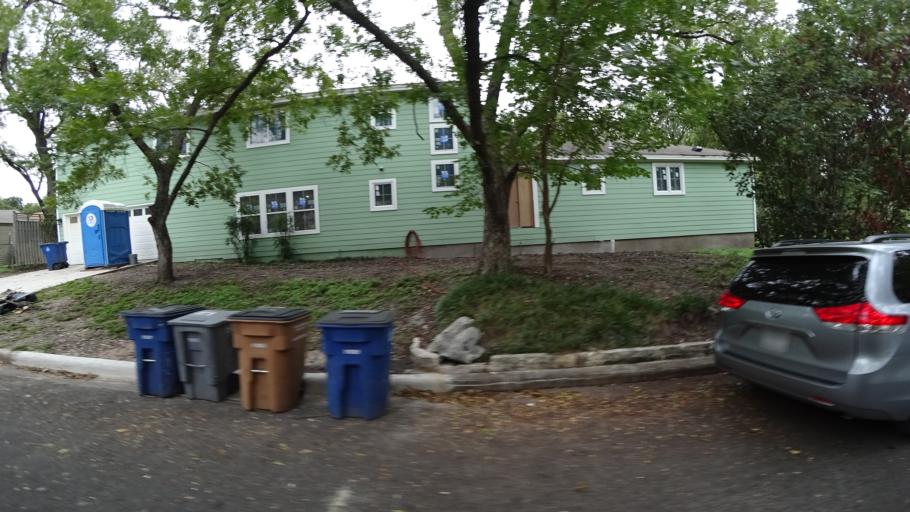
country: US
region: Texas
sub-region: Travis County
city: Austin
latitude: 30.2897
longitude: -97.7195
